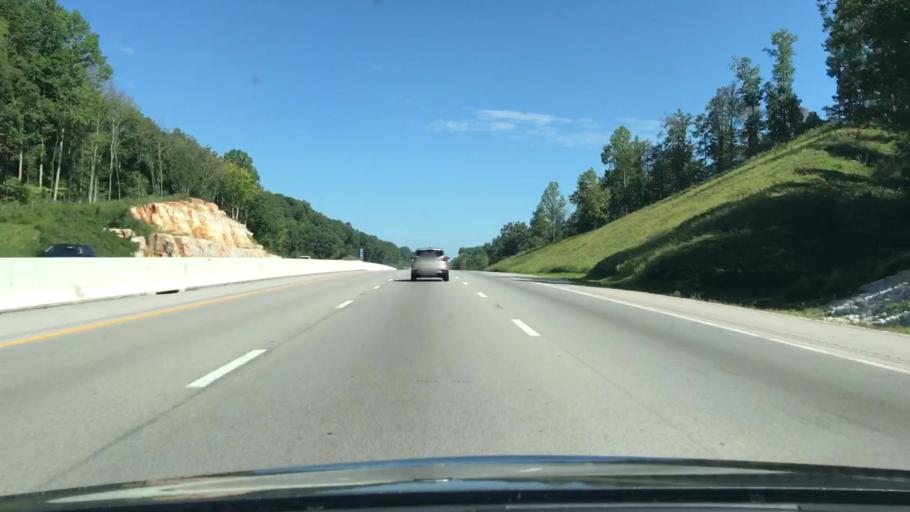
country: US
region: Kentucky
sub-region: Hart County
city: Munfordville
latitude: 37.3060
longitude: -85.9029
